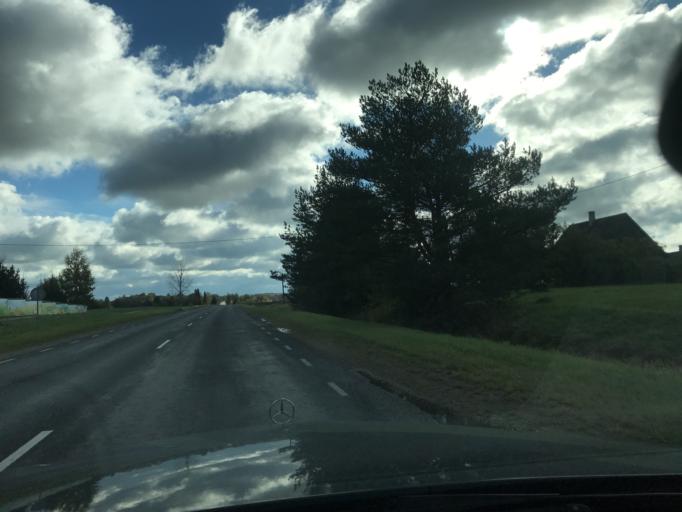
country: EE
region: Vorumaa
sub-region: Antsla vald
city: Vana-Antsla
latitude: 57.9533
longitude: 26.2814
